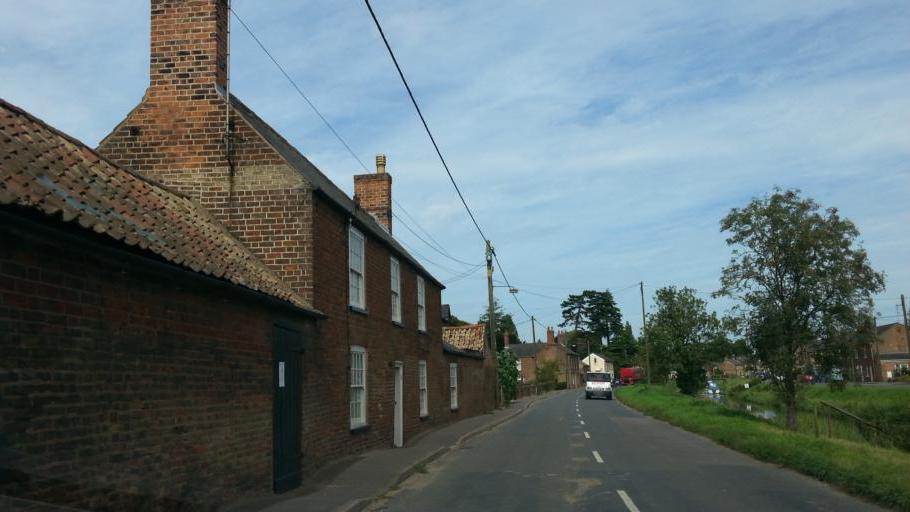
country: GB
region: England
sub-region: Norfolk
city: Outwell
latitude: 52.5998
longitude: 0.2129
